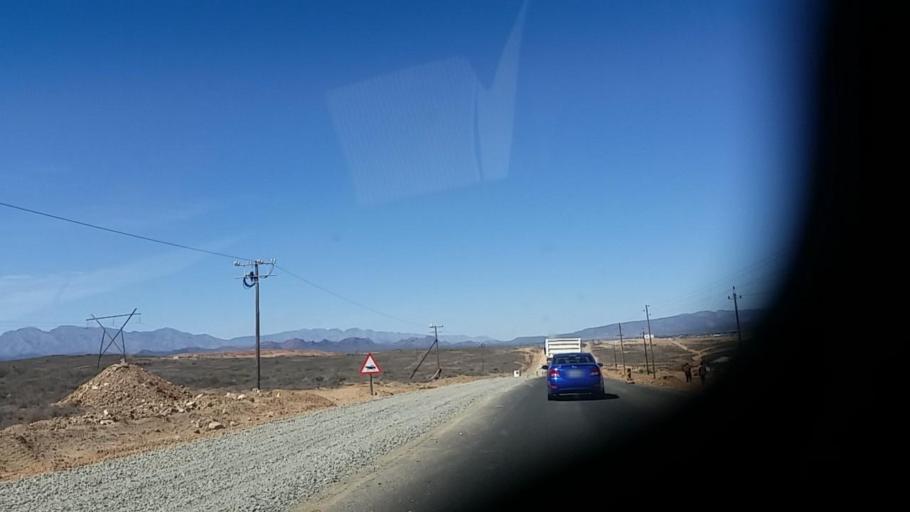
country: ZA
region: Western Cape
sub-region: Eden District Municipality
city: Oudtshoorn
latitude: -33.5914
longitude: 22.2418
